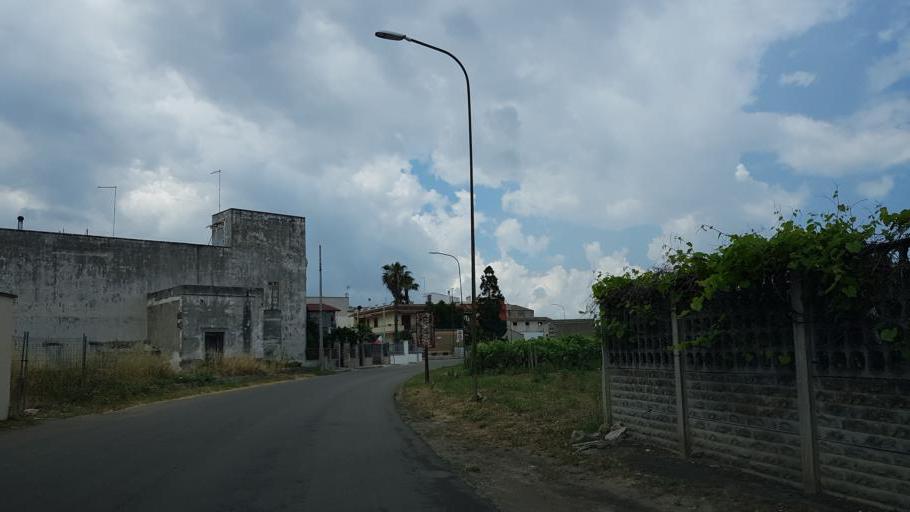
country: IT
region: Apulia
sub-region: Provincia di Brindisi
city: San Donaci
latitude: 40.4519
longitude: 17.9195
